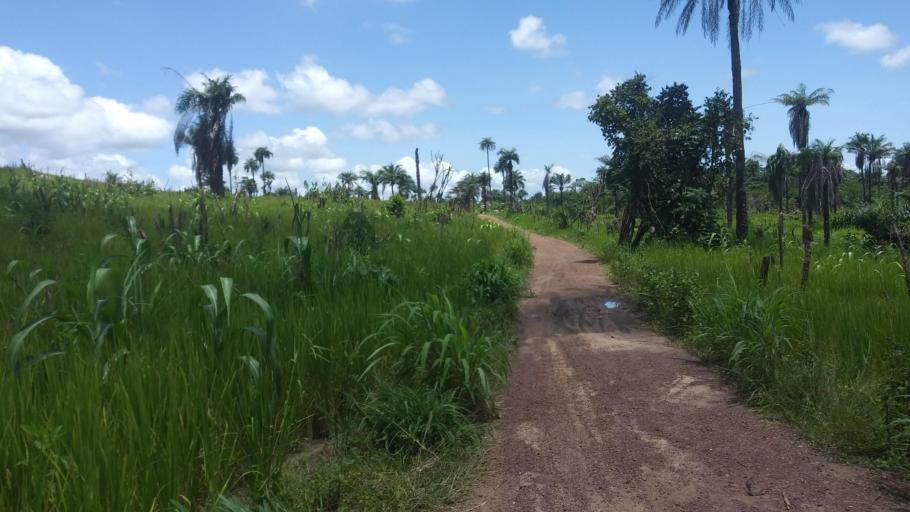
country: SL
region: Northern Province
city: Makeni
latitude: 8.8933
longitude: -12.0043
